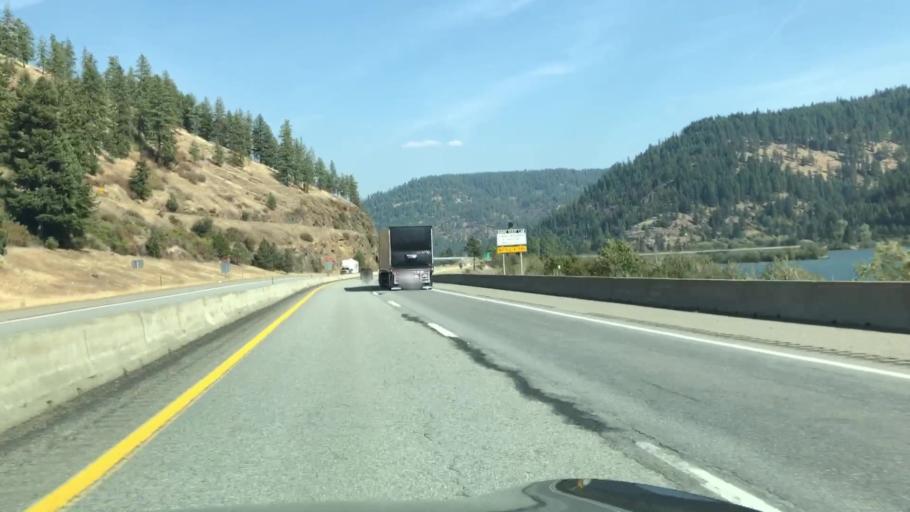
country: US
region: Idaho
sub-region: Kootenai County
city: Coeur d'Alene
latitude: 47.6236
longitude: -116.6592
